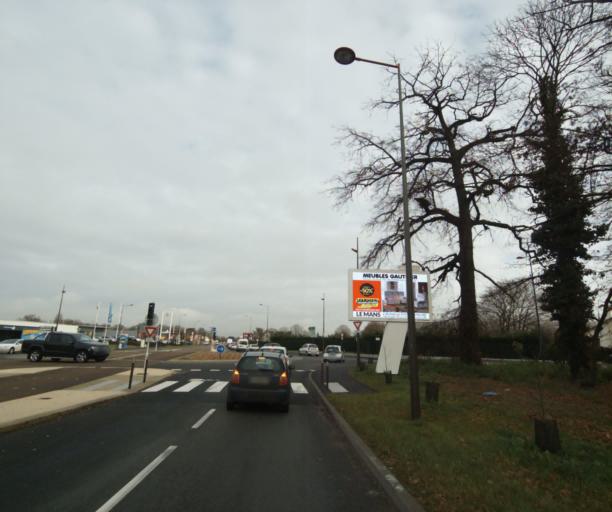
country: FR
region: Pays de la Loire
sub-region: Departement de la Sarthe
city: Allonnes
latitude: 47.9825
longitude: 0.1764
